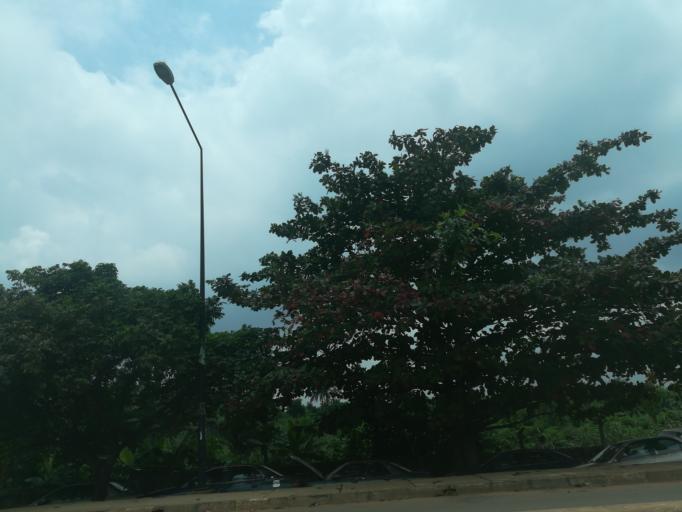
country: NG
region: Lagos
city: Ikorodu
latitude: 6.6240
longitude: 3.5245
